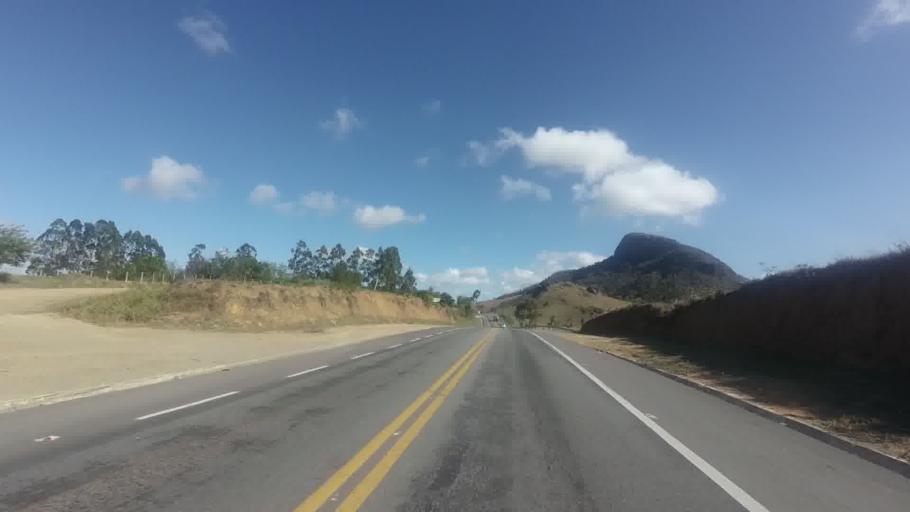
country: BR
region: Espirito Santo
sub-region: Viana
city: Viana
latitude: -20.4885
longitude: -40.4770
